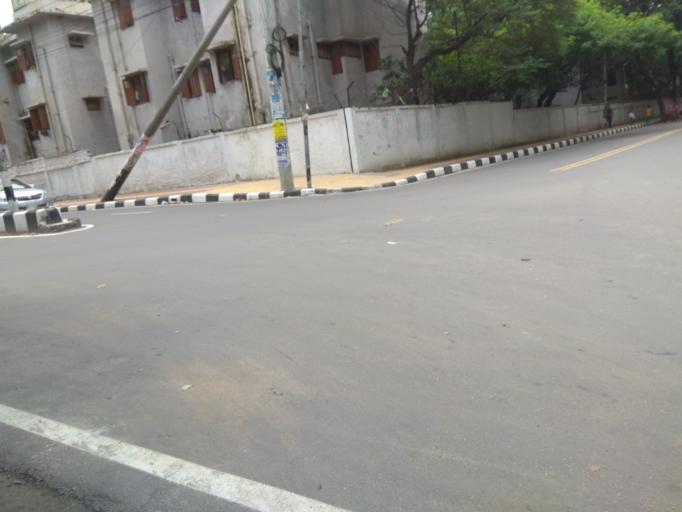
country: BD
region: Dhaka
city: Azimpur
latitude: 23.8026
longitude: 90.3571
